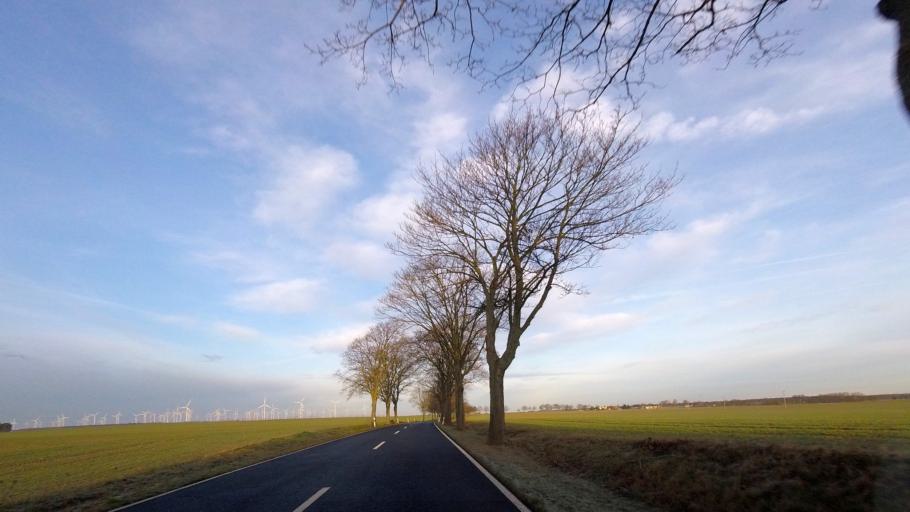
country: DE
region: Brandenburg
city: Niedergorsdorf
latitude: 51.9933
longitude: 12.9398
